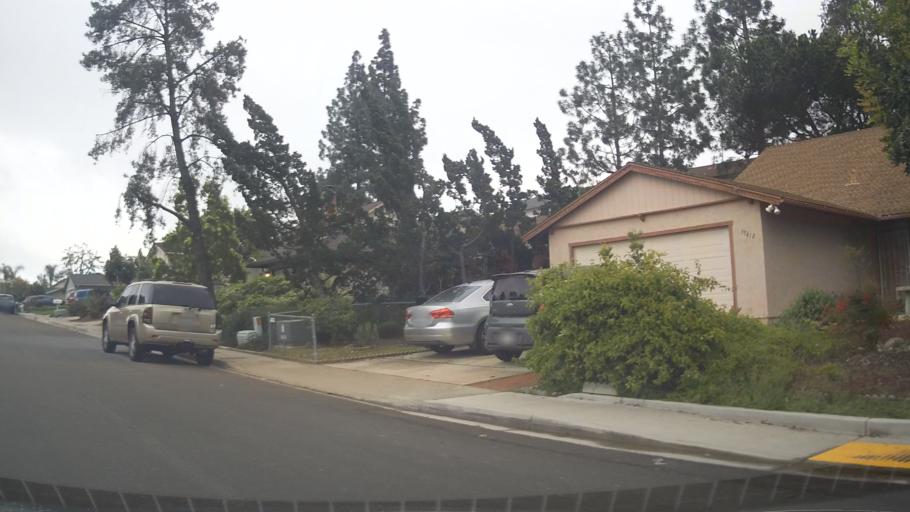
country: US
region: California
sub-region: San Diego County
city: Poway
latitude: 32.9939
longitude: -117.0868
